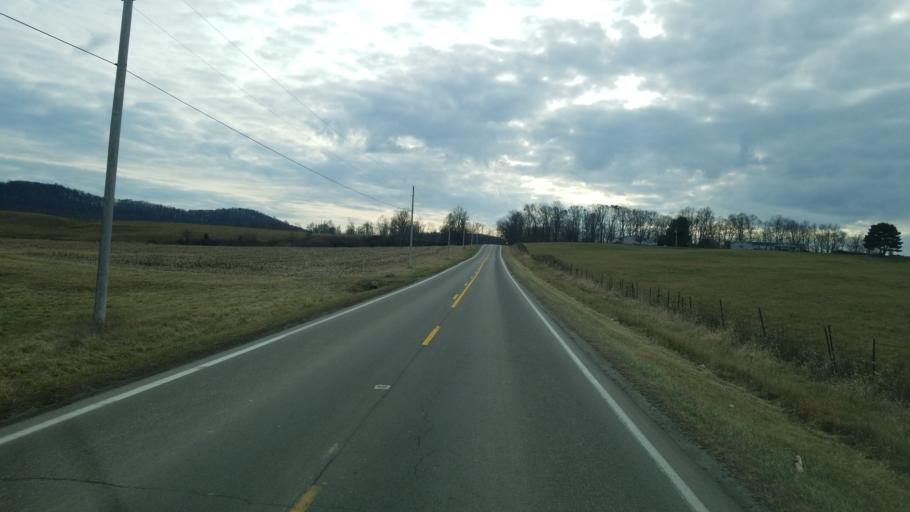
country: US
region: Ohio
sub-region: Highland County
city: Greenfield
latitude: 39.1853
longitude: -83.3401
